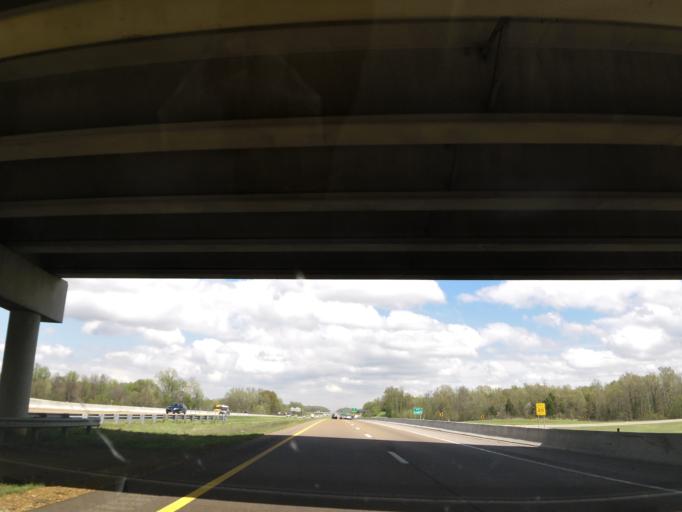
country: US
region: Tennessee
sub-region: Shelby County
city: Arlington
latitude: 35.2558
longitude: -89.6771
